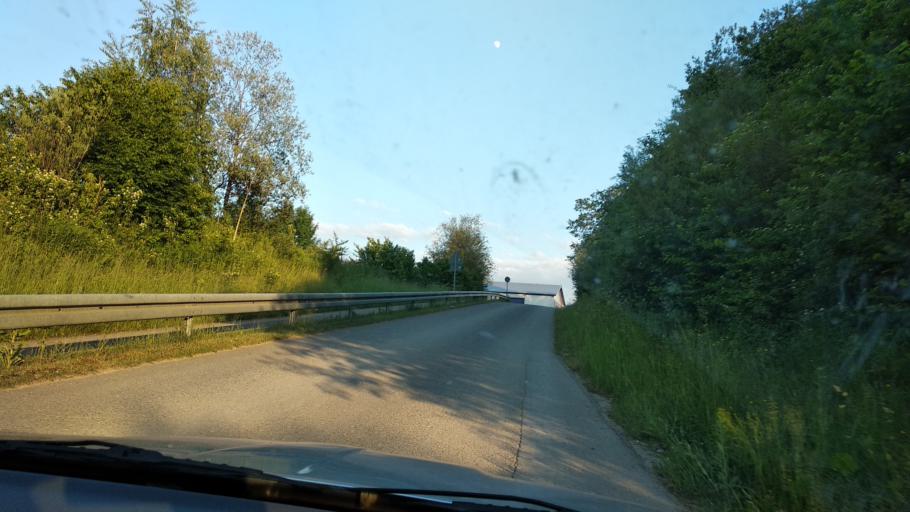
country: DE
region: Baden-Wuerttemberg
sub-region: Tuebingen Region
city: Aitrach
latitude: 47.9304
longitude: 10.0937
